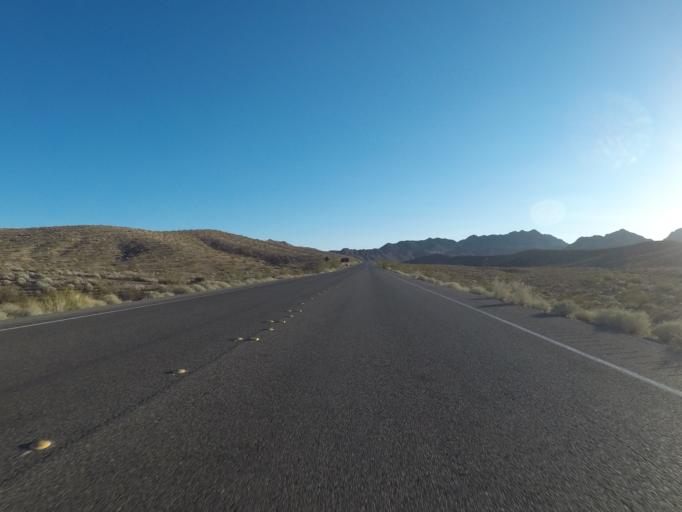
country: US
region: Nevada
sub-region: Clark County
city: Moapa Valley
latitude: 36.2719
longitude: -114.4828
